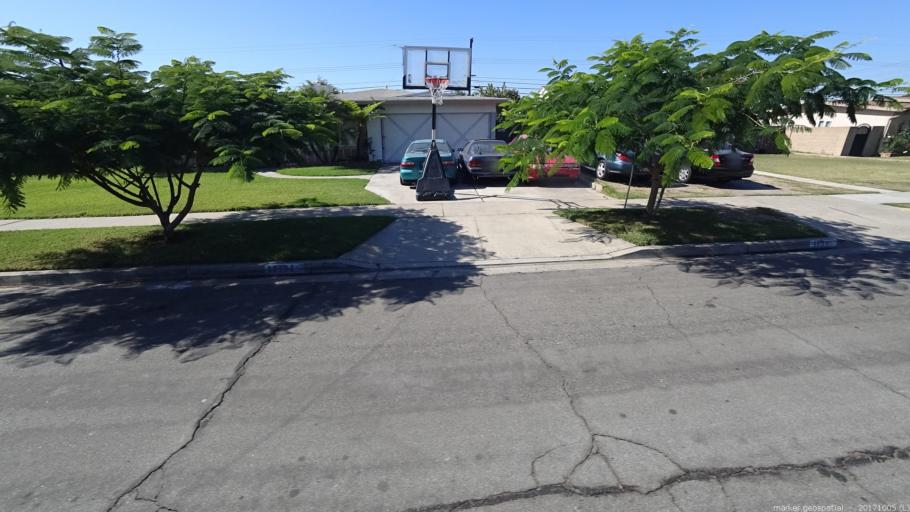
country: US
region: California
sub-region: Orange County
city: Stanton
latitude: 33.7971
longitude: -117.9781
